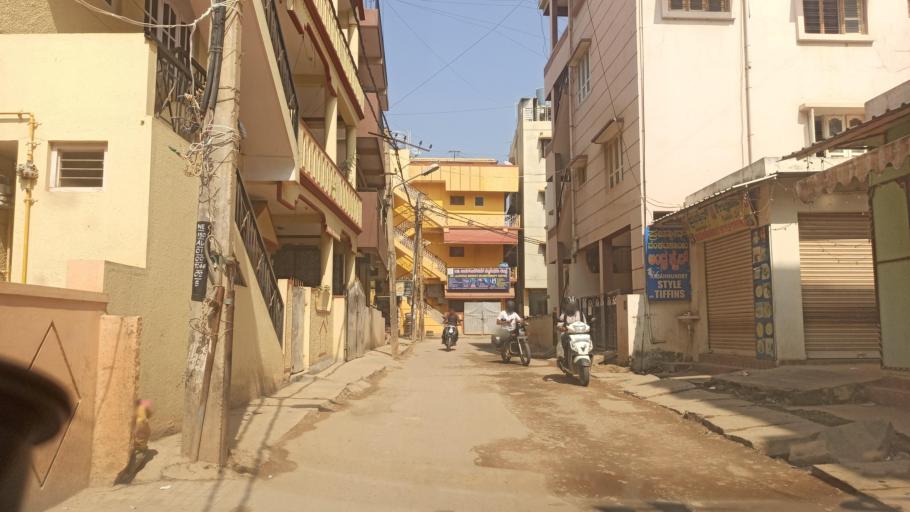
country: IN
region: Karnataka
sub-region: Bangalore Urban
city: Bangalore
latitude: 12.9534
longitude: 77.7043
